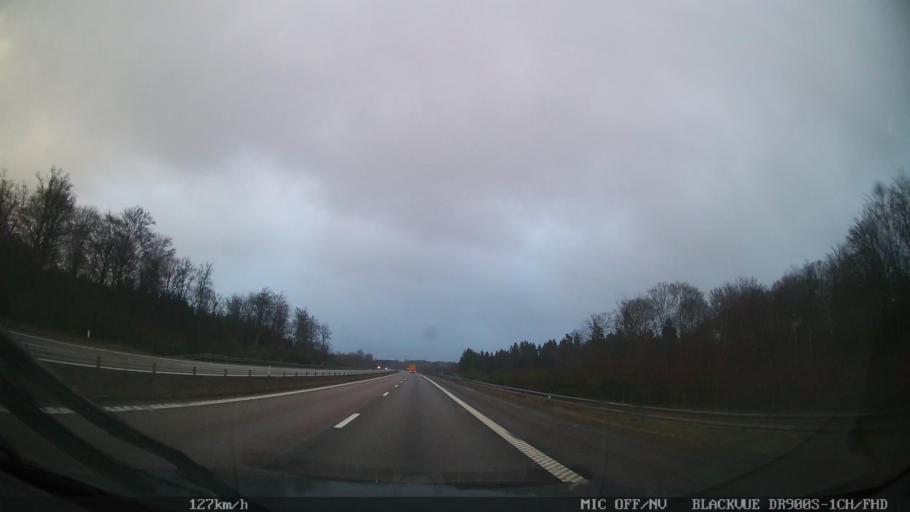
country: SE
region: Skane
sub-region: Orkelljunga Kommun
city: OErkelljunga
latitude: 56.2626
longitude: 13.3036
